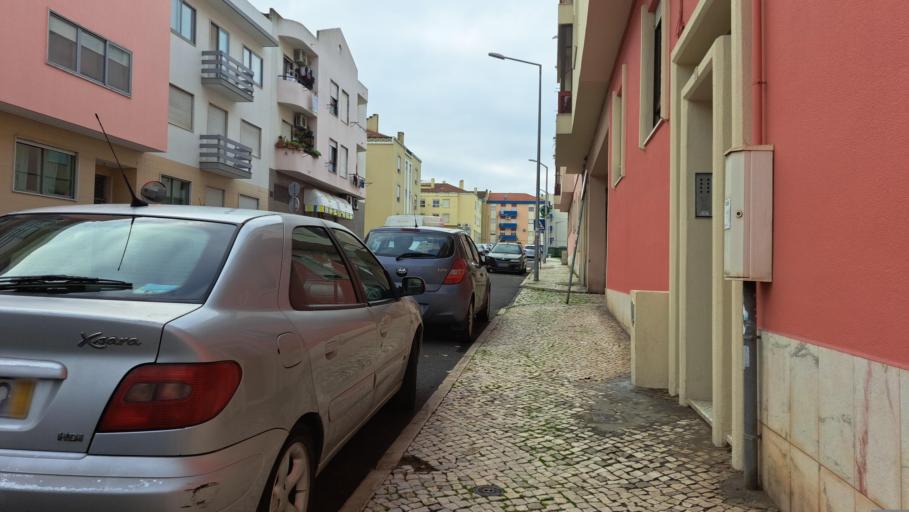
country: PT
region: Setubal
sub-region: Moita
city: Alhos Vedros
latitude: 38.6574
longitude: -9.0467
